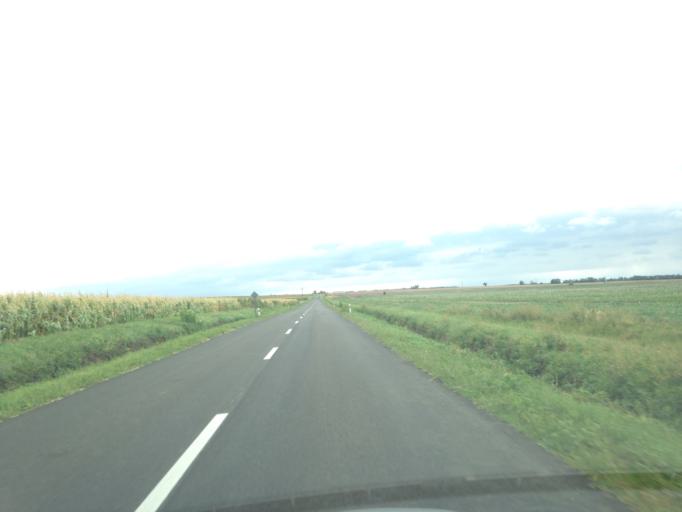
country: SK
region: Nitriansky
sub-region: Okres Komarno
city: Hurbanovo
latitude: 47.9121
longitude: 18.2907
